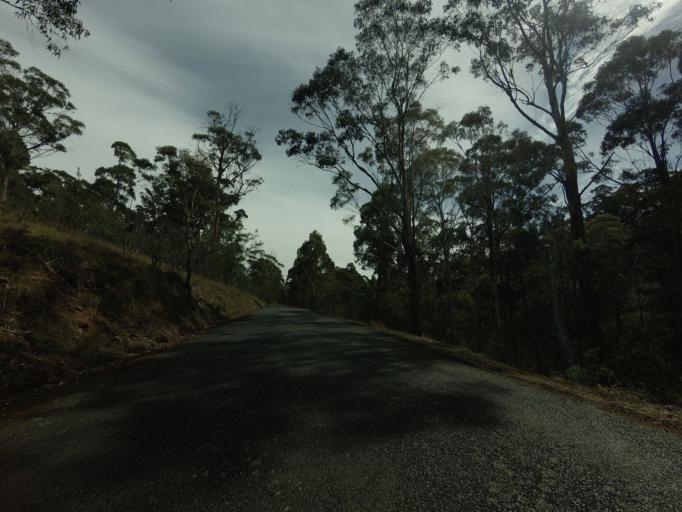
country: AU
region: Tasmania
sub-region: Sorell
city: Sorell
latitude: -42.5618
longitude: 147.6818
